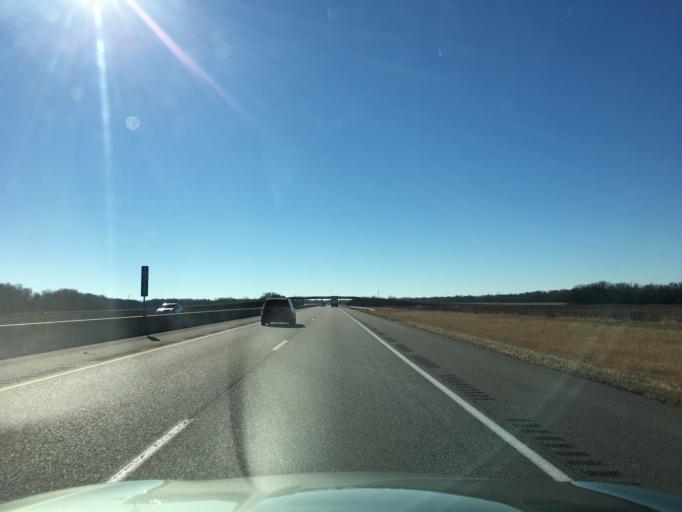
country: US
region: Kansas
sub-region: Sumner County
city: Belle Plaine
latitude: 37.4108
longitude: -97.3226
